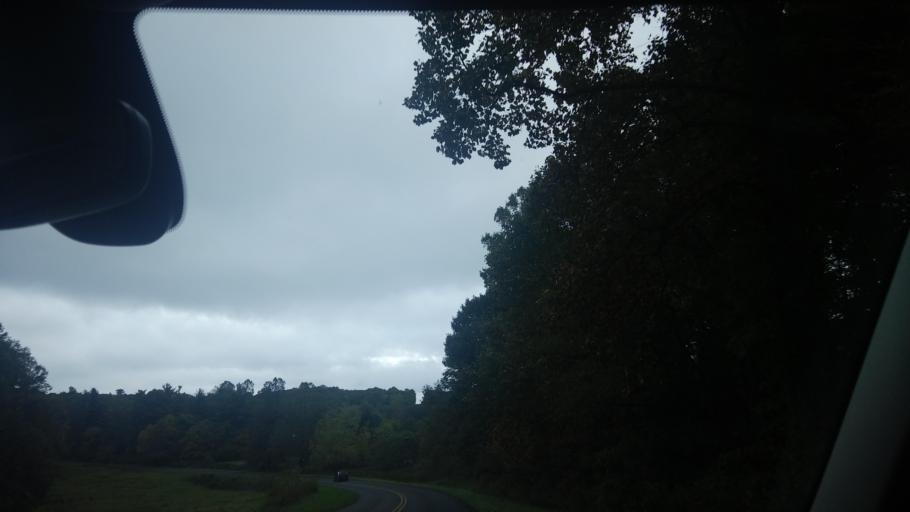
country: US
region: Virginia
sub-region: Carroll County
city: Cana
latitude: 36.6708
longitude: -80.6343
